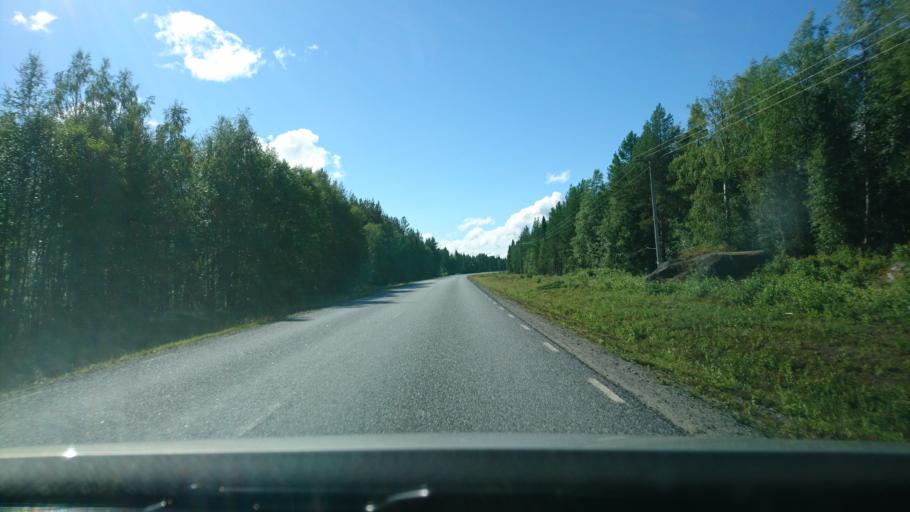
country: SE
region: Vaesterbotten
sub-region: Asele Kommun
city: Asele
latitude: 64.3402
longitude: 17.0306
